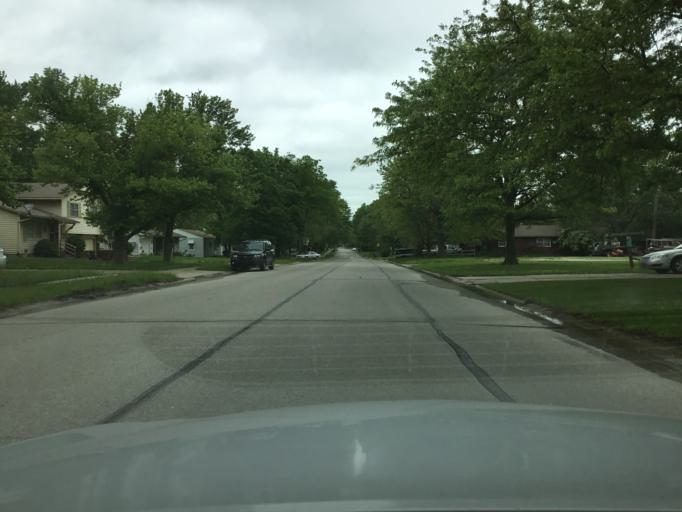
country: US
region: Kansas
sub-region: Franklin County
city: Ottawa
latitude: 38.6015
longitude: -95.2770
